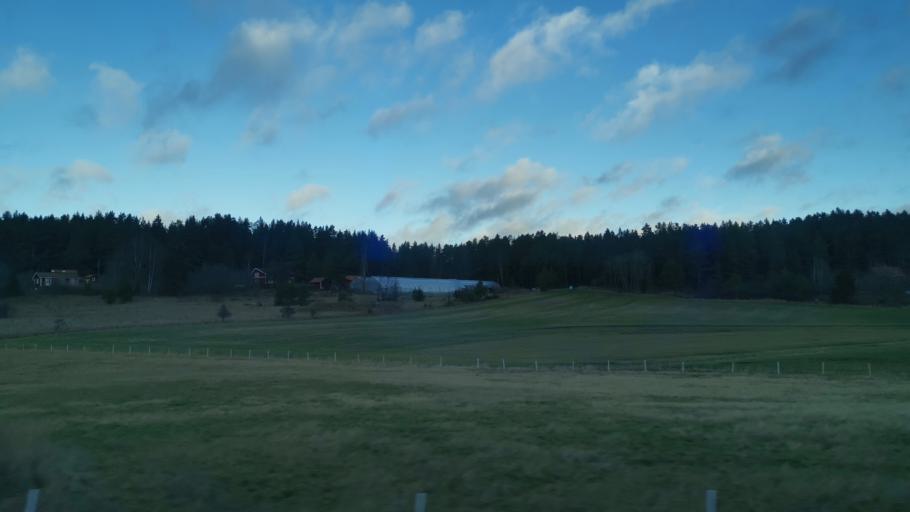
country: SE
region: Soedermanland
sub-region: Gnesta Kommun
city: Gnesta
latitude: 59.0579
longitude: 17.2039
